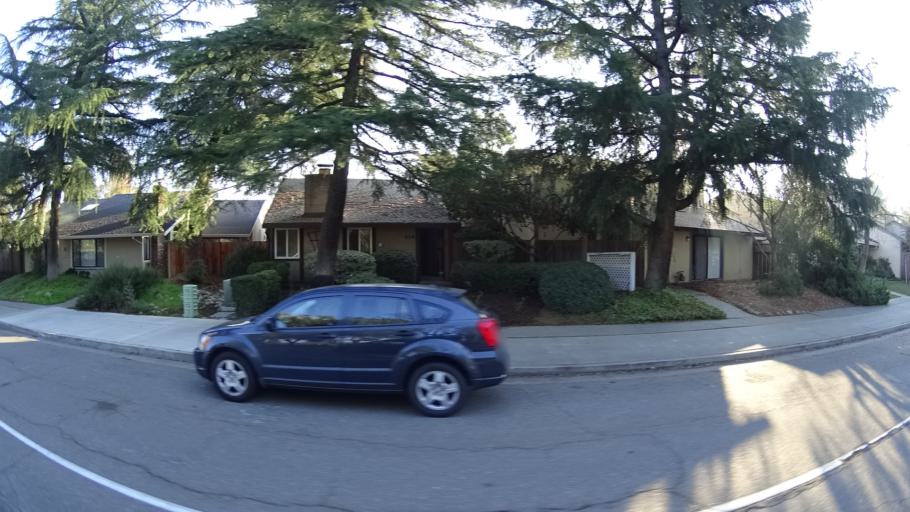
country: US
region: California
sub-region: Yolo County
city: Davis
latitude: 38.5511
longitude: -121.7873
